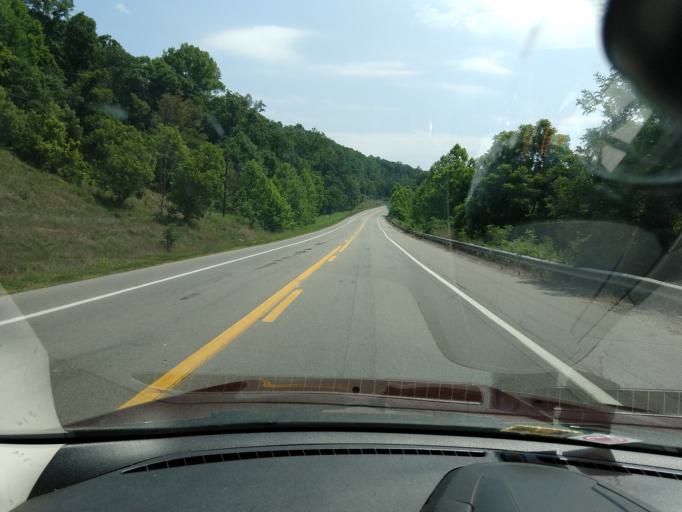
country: US
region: West Virginia
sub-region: Jackson County
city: Ravenswood
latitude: 38.8598
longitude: -81.8136
